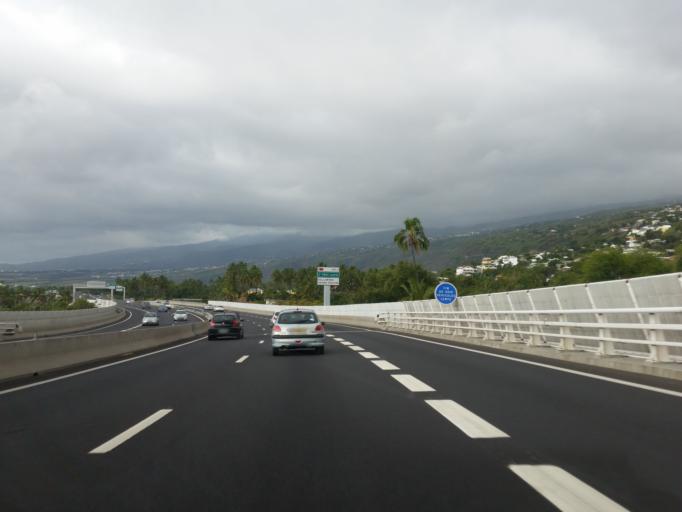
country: RE
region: Reunion
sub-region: Reunion
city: Saint-Paul
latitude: -21.0150
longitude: 55.2707
